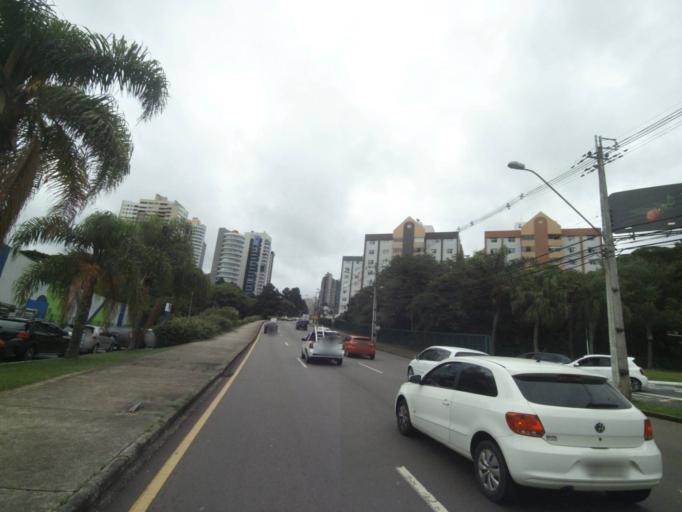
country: BR
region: Parana
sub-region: Curitiba
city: Curitiba
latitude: -25.4367
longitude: -49.3185
